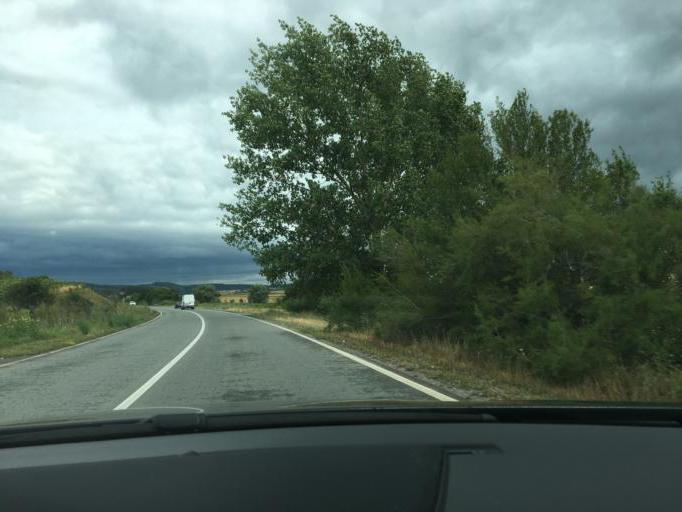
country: BG
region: Kyustendil
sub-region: Obshtina Dupnitsa
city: Dupnitsa
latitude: 42.2732
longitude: 23.0251
